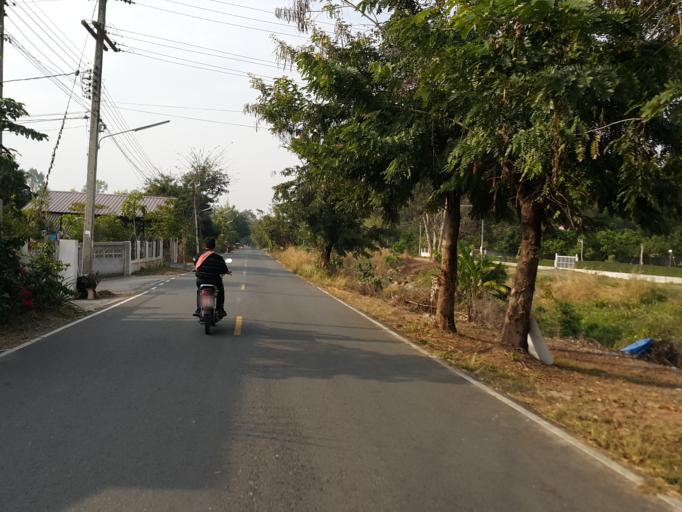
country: TH
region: Chiang Mai
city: San Sai
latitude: 18.8653
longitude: 99.1409
